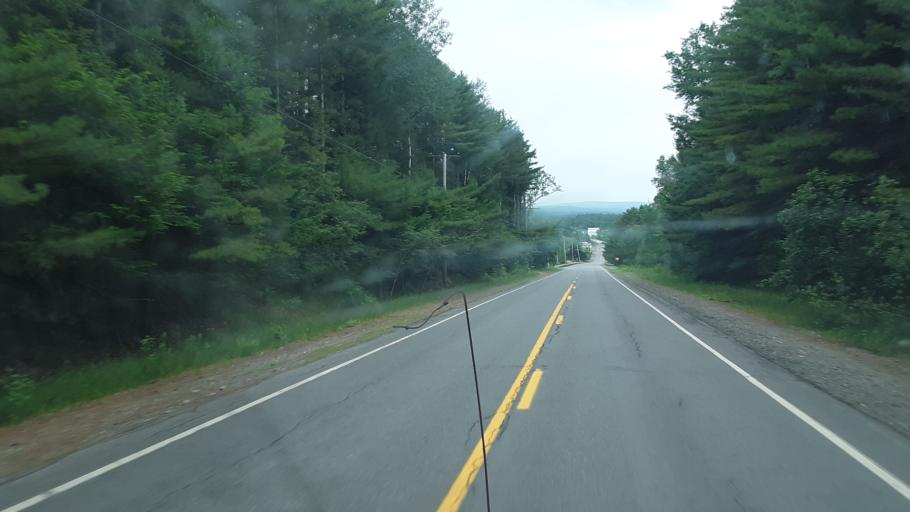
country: US
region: Maine
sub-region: Penobscot County
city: Medway
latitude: 45.5270
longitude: -68.3484
